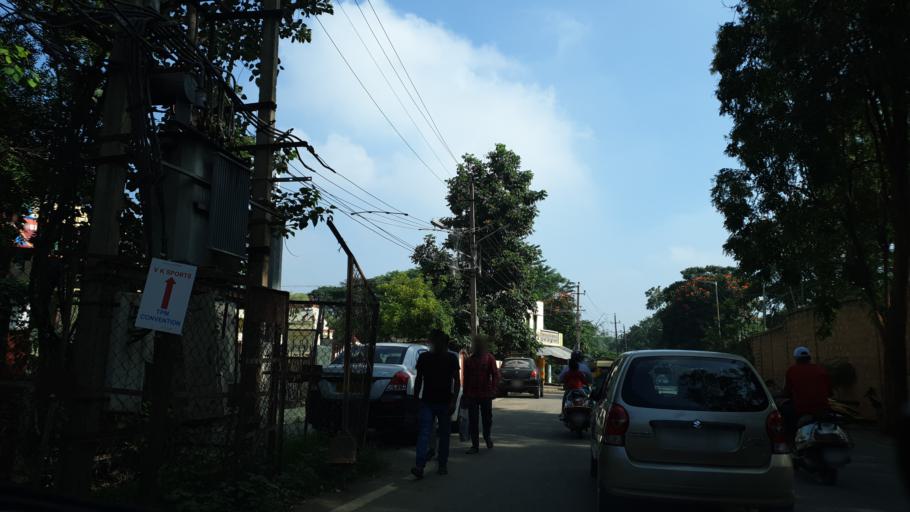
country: IN
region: Karnataka
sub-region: Bangalore Urban
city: Bangalore
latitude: 12.9625
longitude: 77.6817
